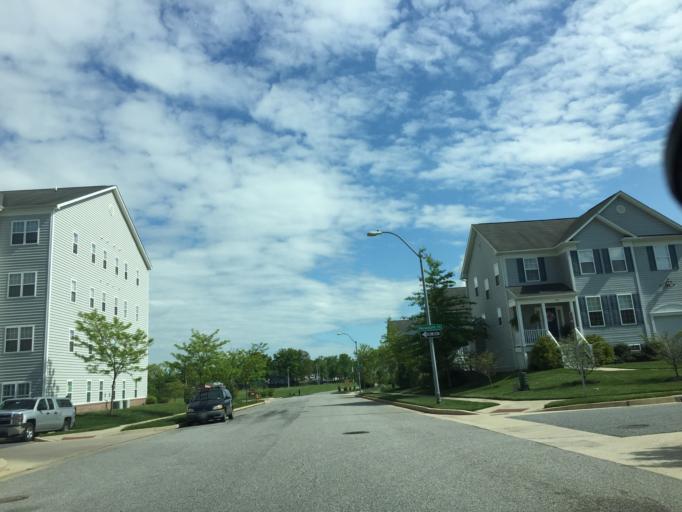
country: US
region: Maryland
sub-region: Baltimore County
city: Middle River
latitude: 39.3147
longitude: -76.4383
